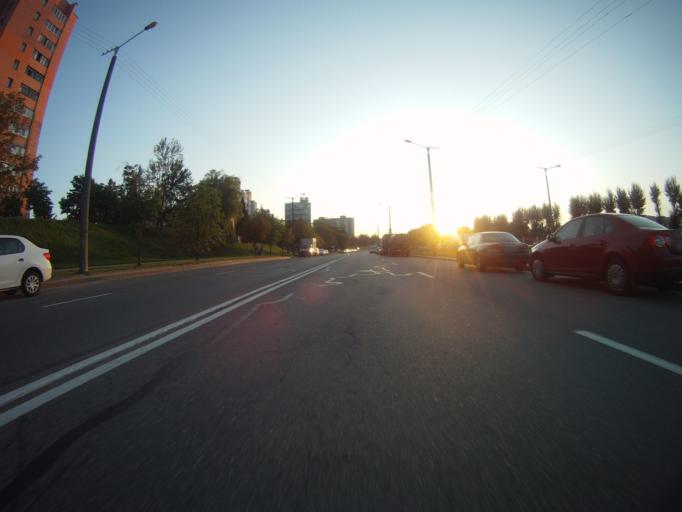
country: BY
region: Minsk
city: Novoye Medvezhino
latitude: 53.9283
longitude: 27.4866
